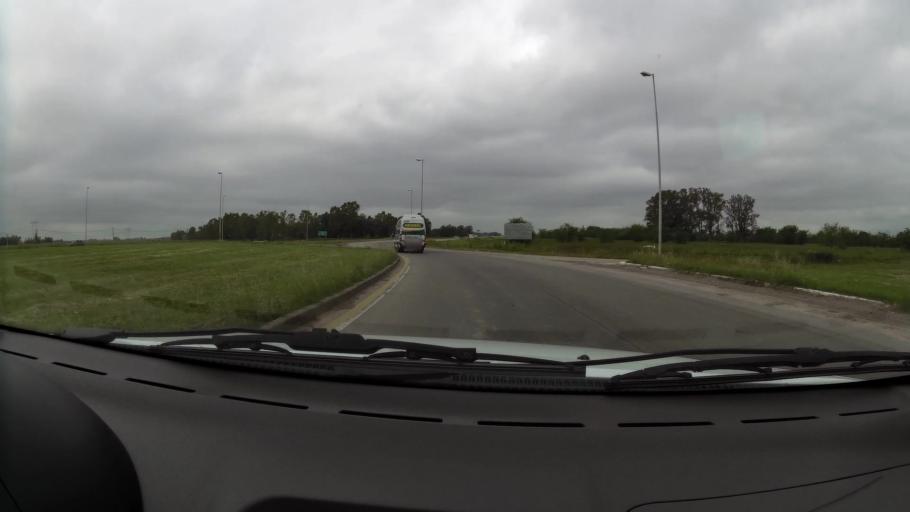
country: AR
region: Buenos Aires
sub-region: Partido de Brandsen
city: Brandsen
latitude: -35.0262
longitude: -58.2297
